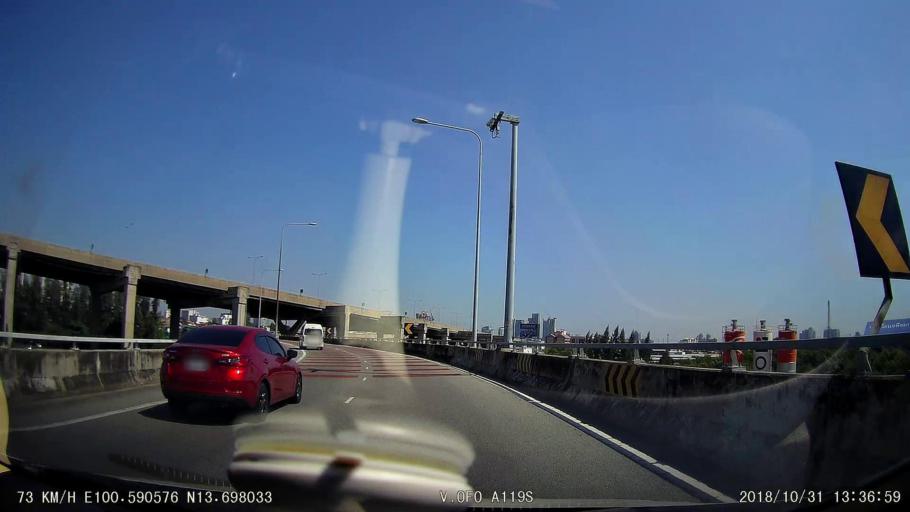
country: TH
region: Bangkok
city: Phra Khanong
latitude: 13.6980
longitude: 100.5907
